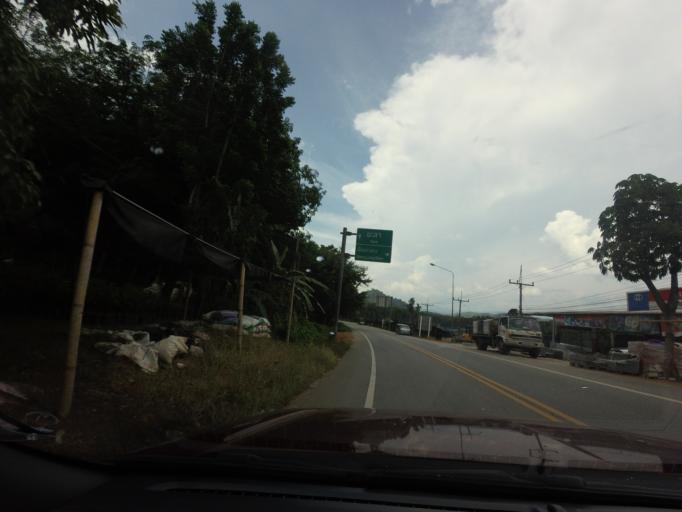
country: TH
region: Yala
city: Ban Nang Sata
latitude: 6.2335
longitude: 101.2121
